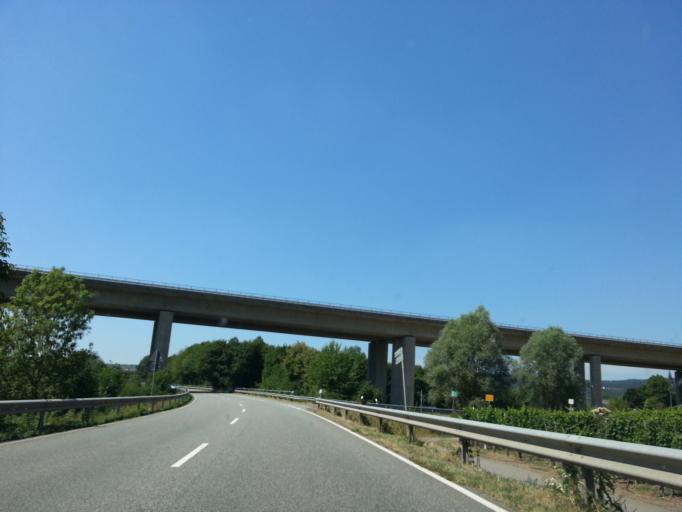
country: DE
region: Rheinland-Pfalz
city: Schweich
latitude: 49.8160
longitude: 6.7599
